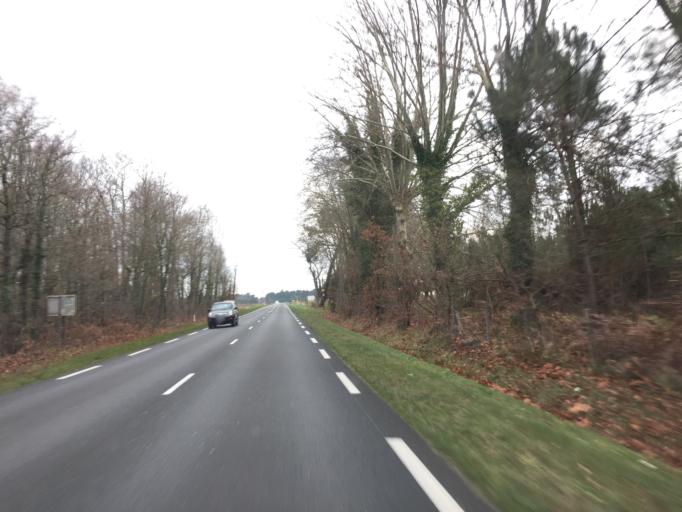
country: FR
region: Aquitaine
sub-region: Departement de la Gironde
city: Saint-Sauveur
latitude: 45.1663
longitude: -0.8326
